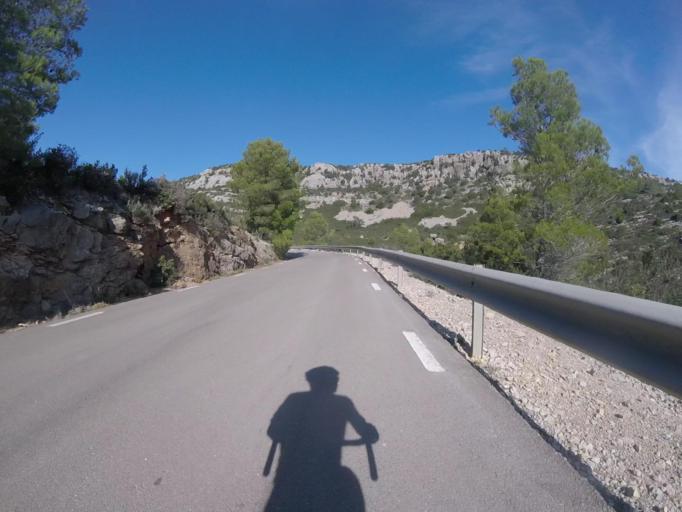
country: ES
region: Valencia
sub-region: Provincia de Castello
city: Sarratella
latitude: 40.2724
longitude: 0.0486
